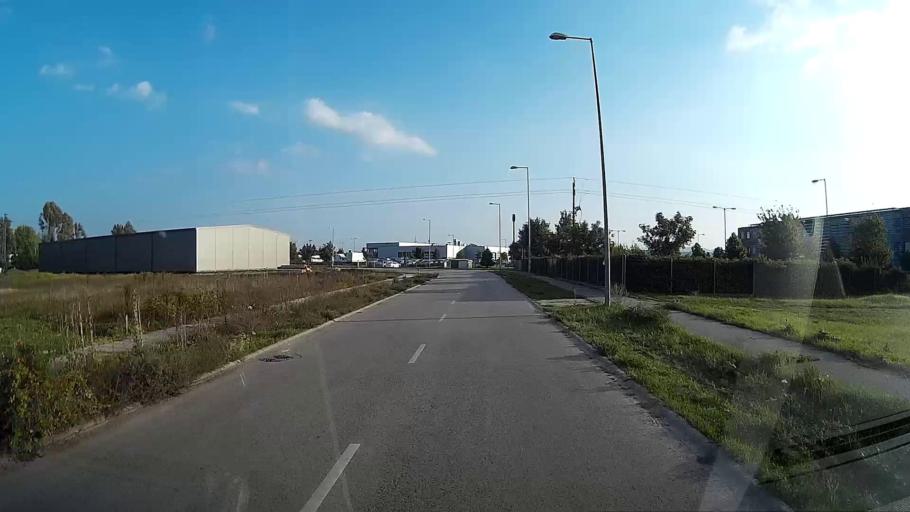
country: HU
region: Pest
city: Szentendre
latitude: 47.6424
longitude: 19.0655
